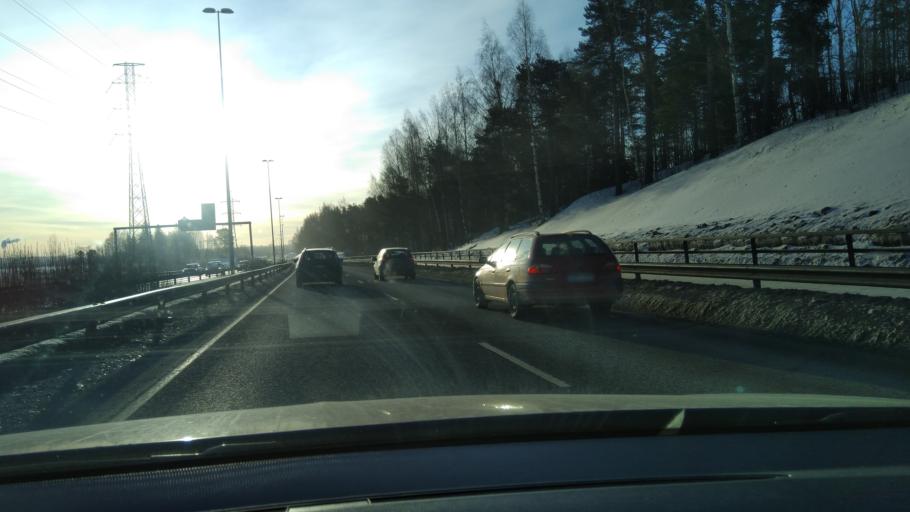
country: FI
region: Pirkanmaa
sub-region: Tampere
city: Pirkkala
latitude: 61.5089
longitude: 23.6947
